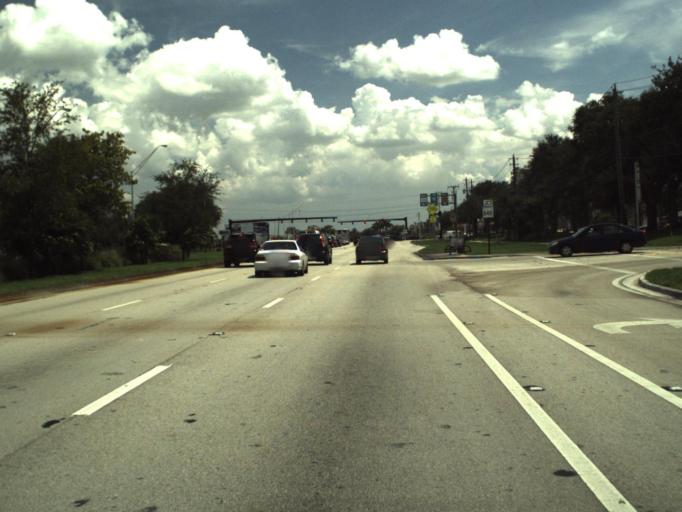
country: US
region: Florida
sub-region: Broward County
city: Cooper City
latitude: 26.0478
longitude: -80.2519
